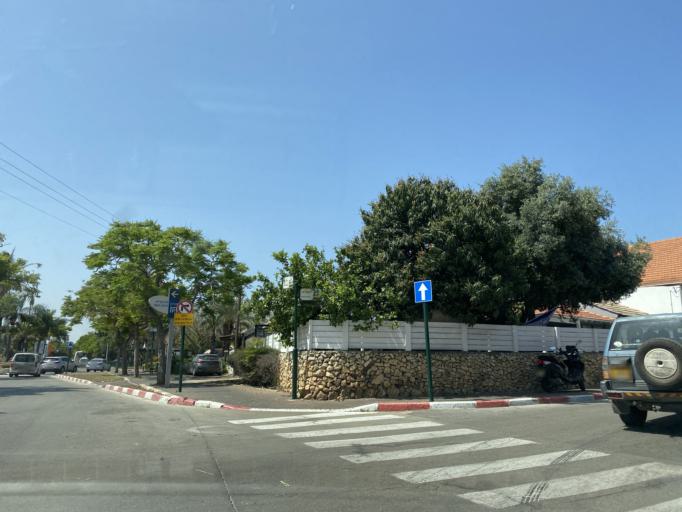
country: IL
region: Central District
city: Ra'anana
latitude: 32.1915
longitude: 34.8739
